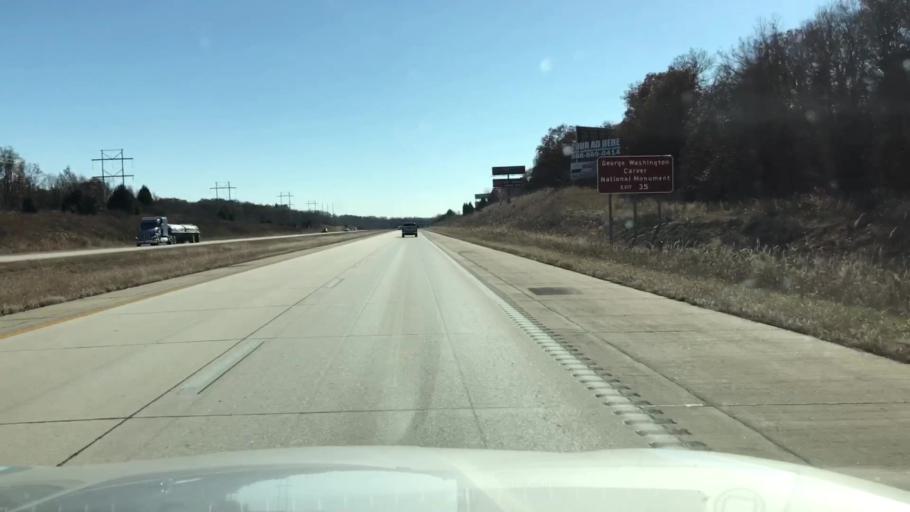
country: US
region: Missouri
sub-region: Jasper County
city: Duquesne
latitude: 37.0086
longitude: -94.4307
